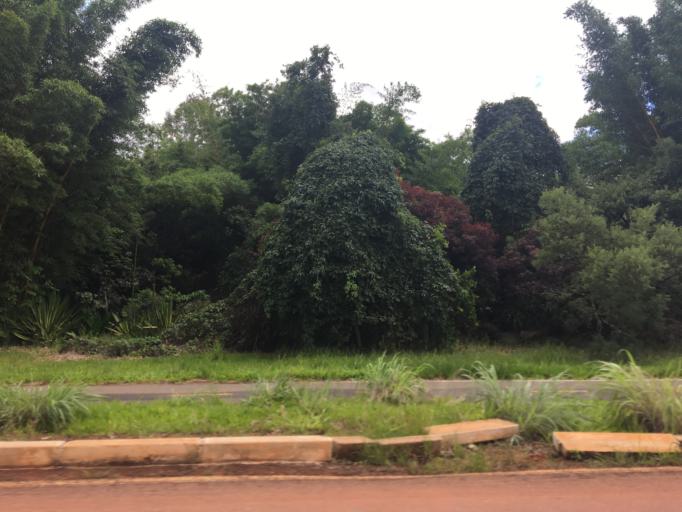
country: BR
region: Federal District
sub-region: Brasilia
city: Brasilia
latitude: -15.8988
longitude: -47.9280
